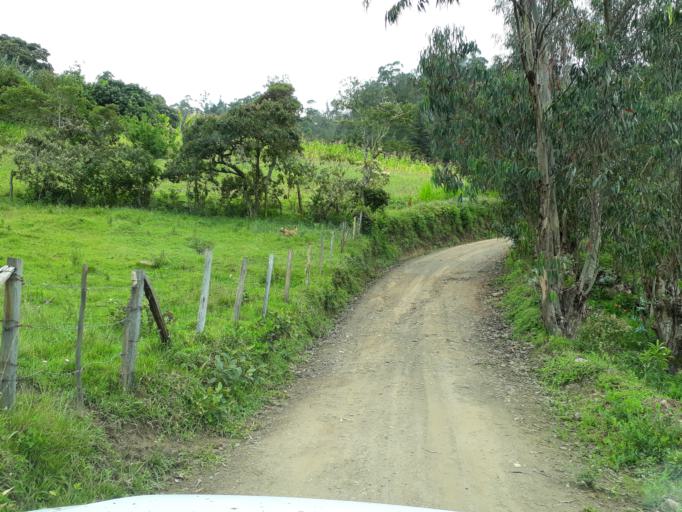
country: CO
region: Cundinamarca
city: Junin
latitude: 4.7808
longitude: -73.6416
